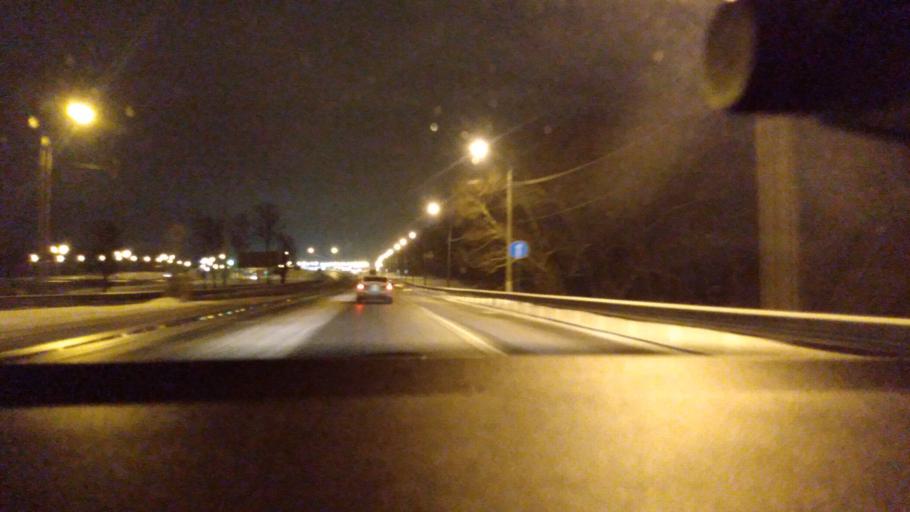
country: RU
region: Moskovskaya
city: Raduzhnyy
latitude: 55.1682
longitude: 38.6692
